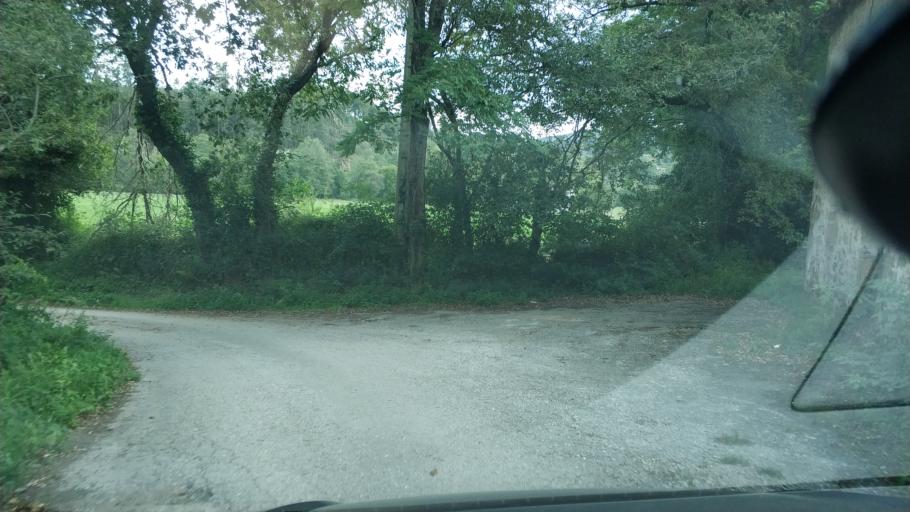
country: ES
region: Cantabria
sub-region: Provincia de Cantabria
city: Santa Maria de Cayon
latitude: 43.2955
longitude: -3.8546
